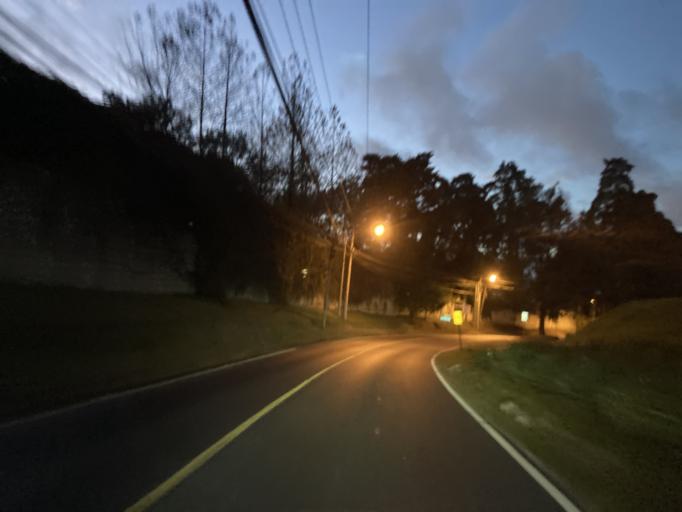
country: GT
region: Guatemala
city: Santa Catarina Pinula
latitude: 14.6024
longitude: -90.4670
